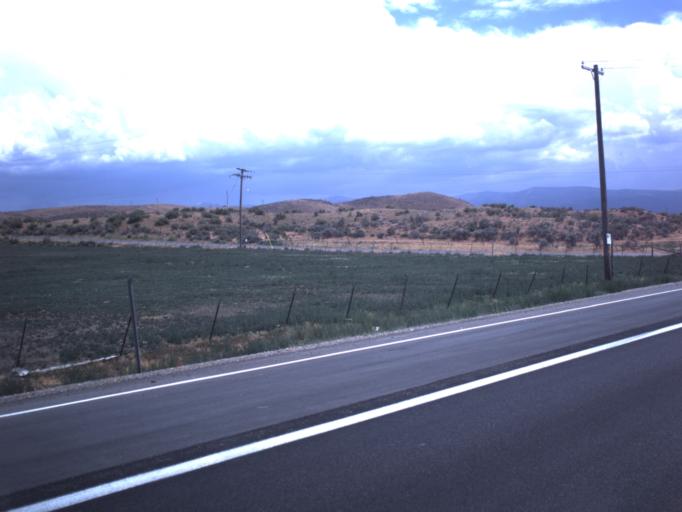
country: US
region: Utah
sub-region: Sanpete County
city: Moroni
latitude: 39.5576
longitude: -111.6009
